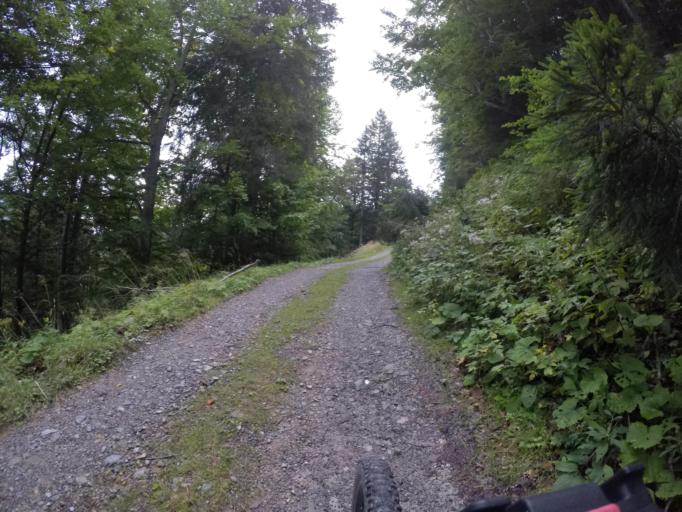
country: IT
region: Friuli Venezia Giulia
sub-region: Provincia di Udine
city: Pontebba
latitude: 46.5163
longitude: 13.2407
